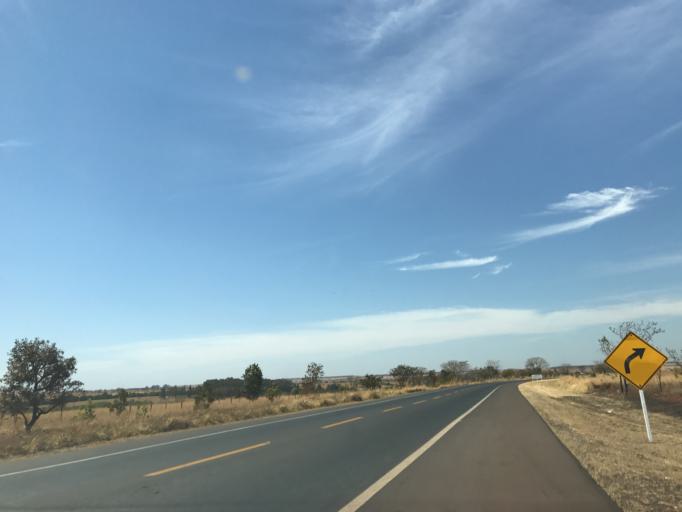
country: BR
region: Minas Gerais
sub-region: Monte Alegre De Minas
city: Monte Alegre de Minas
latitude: -18.9127
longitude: -49.0365
